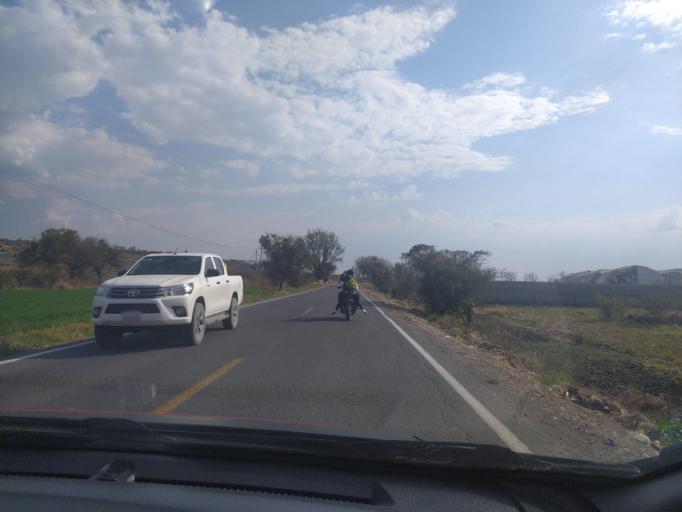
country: MX
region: Guanajuato
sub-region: San Francisco del Rincon
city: San Ignacio de Hidalgo
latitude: 20.8782
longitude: -101.8595
